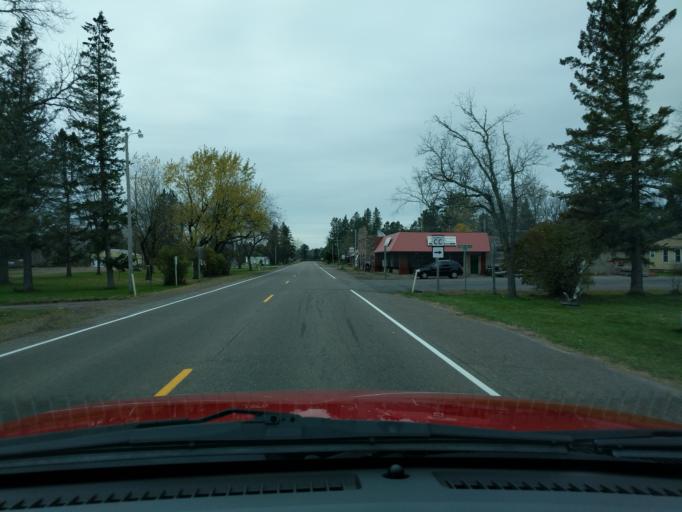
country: US
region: Wisconsin
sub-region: Sawyer County
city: Little Round Lake
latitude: 45.7959
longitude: -91.3052
